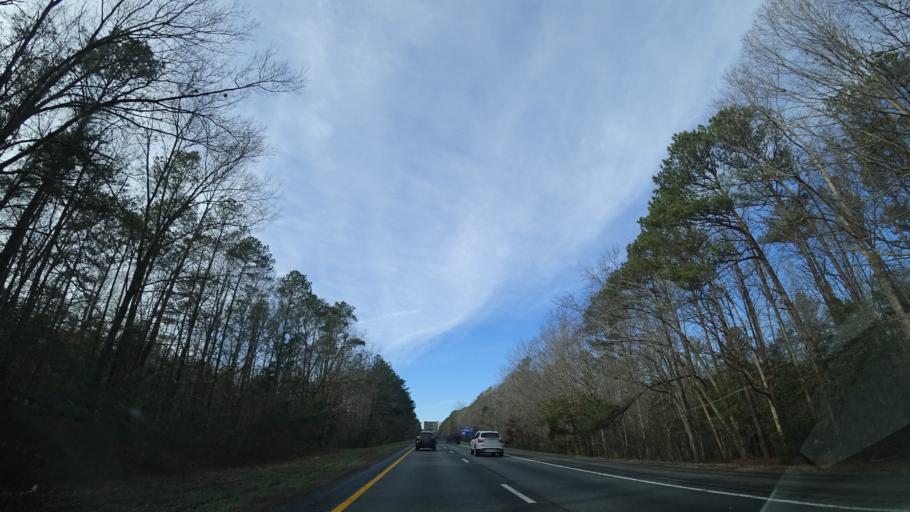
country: US
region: Virginia
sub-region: New Kent County
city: New Kent
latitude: 37.4915
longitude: -77.0047
